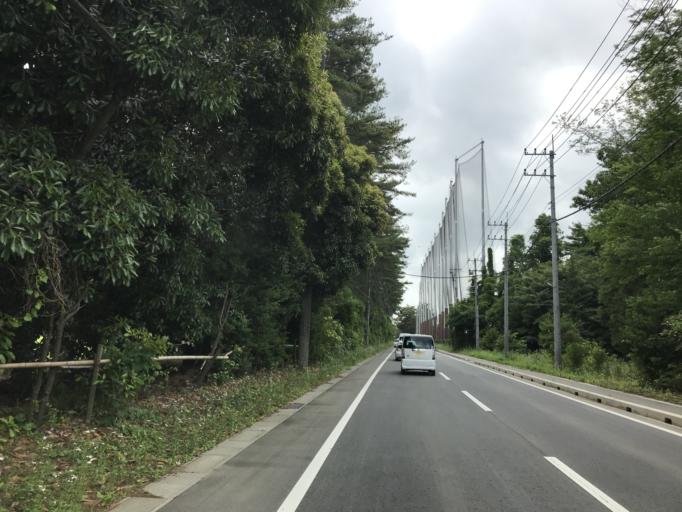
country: JP
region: Ibaraki
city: Ushiku
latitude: 35.9797
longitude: 140.0682
